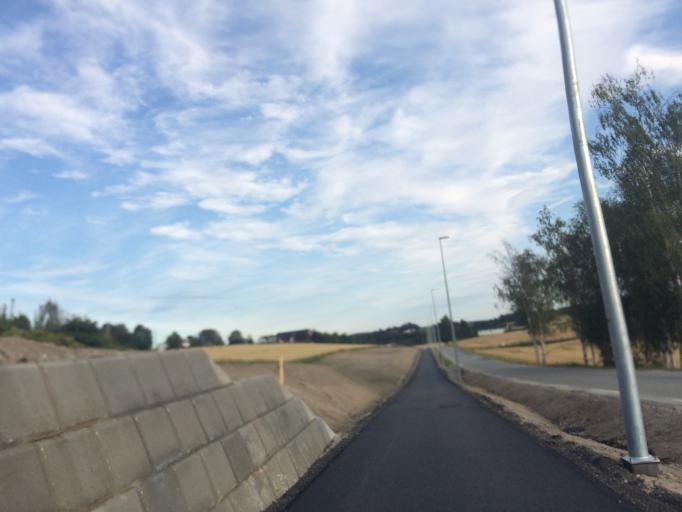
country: NO
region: Akershus
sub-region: Ski
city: Ski
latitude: 59.6925
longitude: 10.8611
